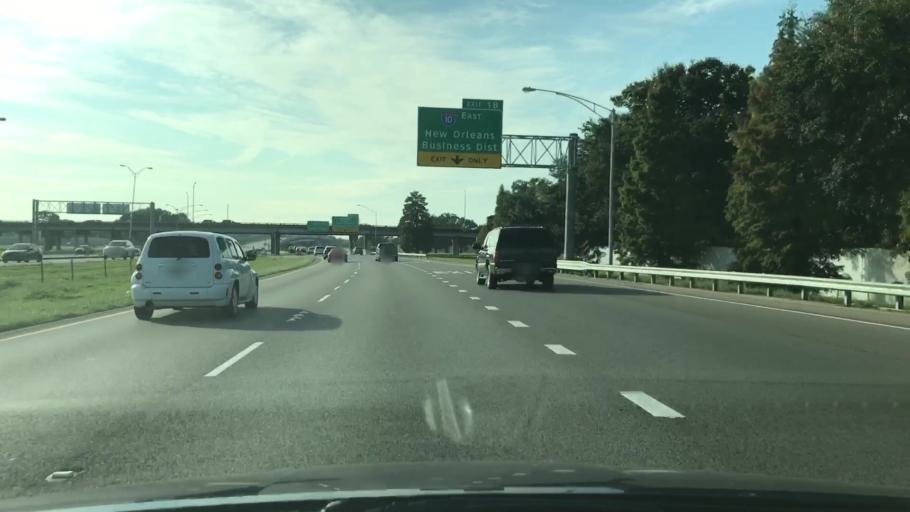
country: US
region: Louisiana
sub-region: Jefferson Parish
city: Metairie
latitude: 29.9956
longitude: -90.1135
